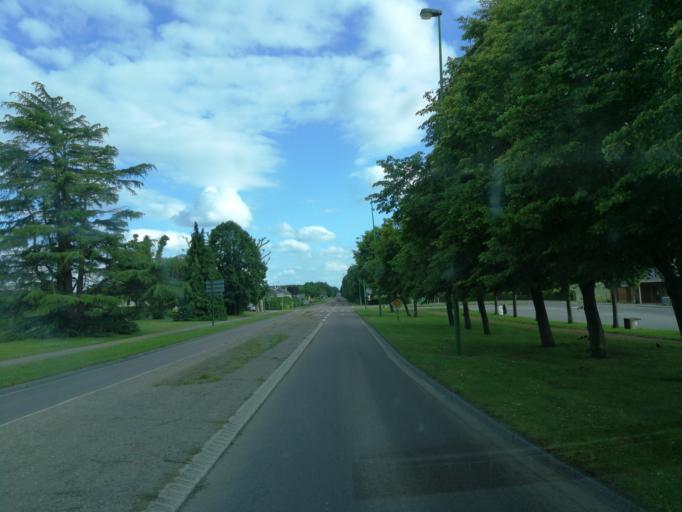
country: FR
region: Haute-Normandie
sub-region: Departement de l'Eure
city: Le Neubourg
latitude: 49.1411
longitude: 0.9033
